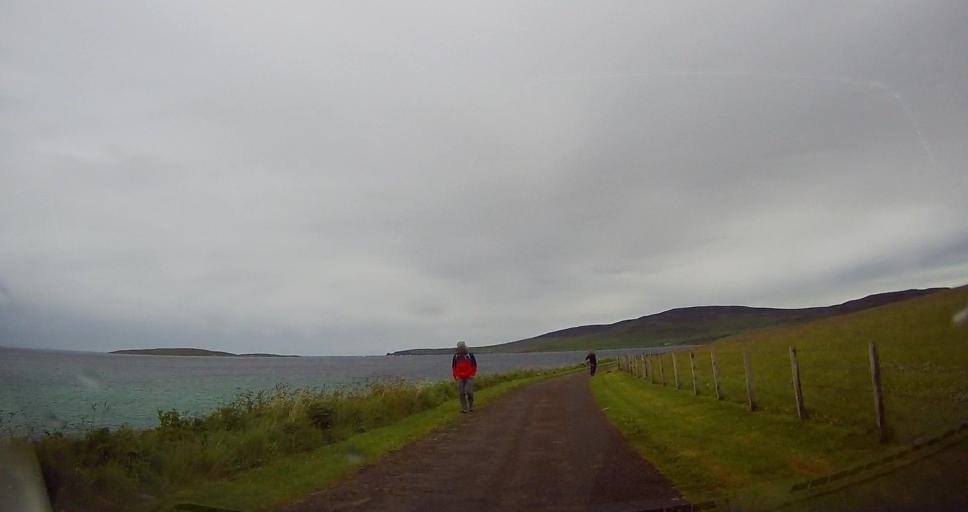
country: GB
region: Scotland
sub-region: Orkney Islands
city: Orkney
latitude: 59.1220
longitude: -3.0852
